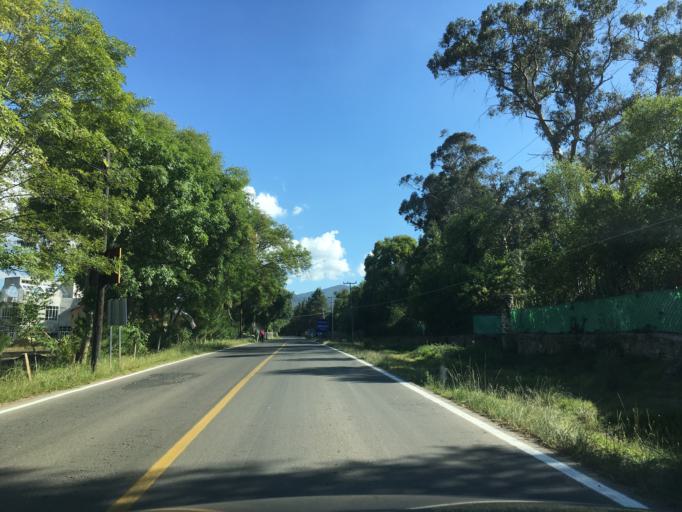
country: MX
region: Hidalgo
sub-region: Omitlan de Juarez
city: San Antonio el Paso
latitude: 20.2160
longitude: -98.5653
